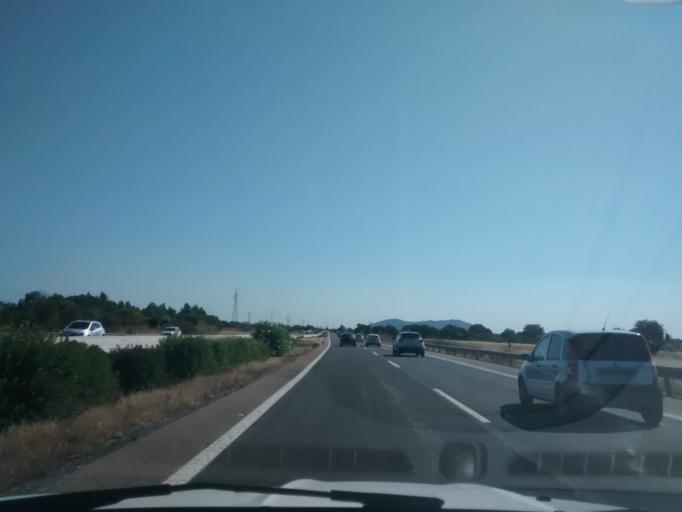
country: ES
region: Balearic Islands
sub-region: Illes Balears
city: Lloseta
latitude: 39.6931
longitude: 2.8746
